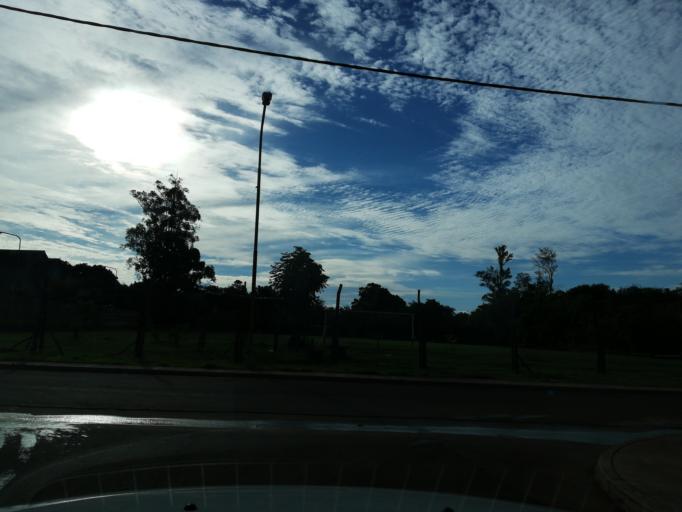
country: AR
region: Misiones
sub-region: Departamento de Capital
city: Posadas
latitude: -27.3969
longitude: -55.9511
